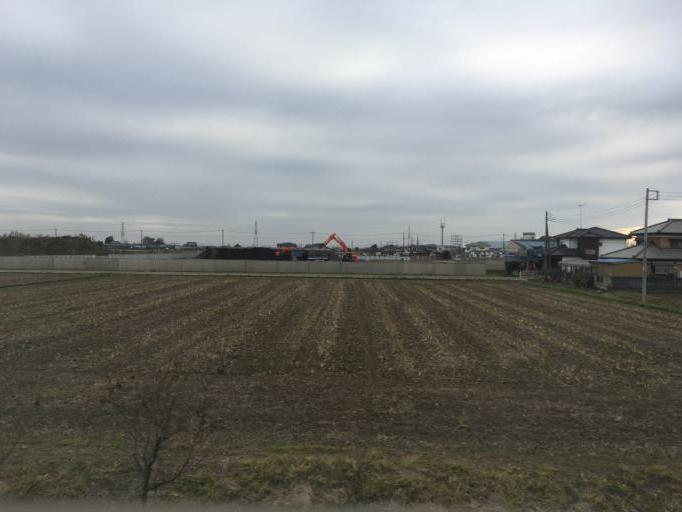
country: JP
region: Tochigi
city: Oyama
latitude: 36.3489
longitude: 139.7853
